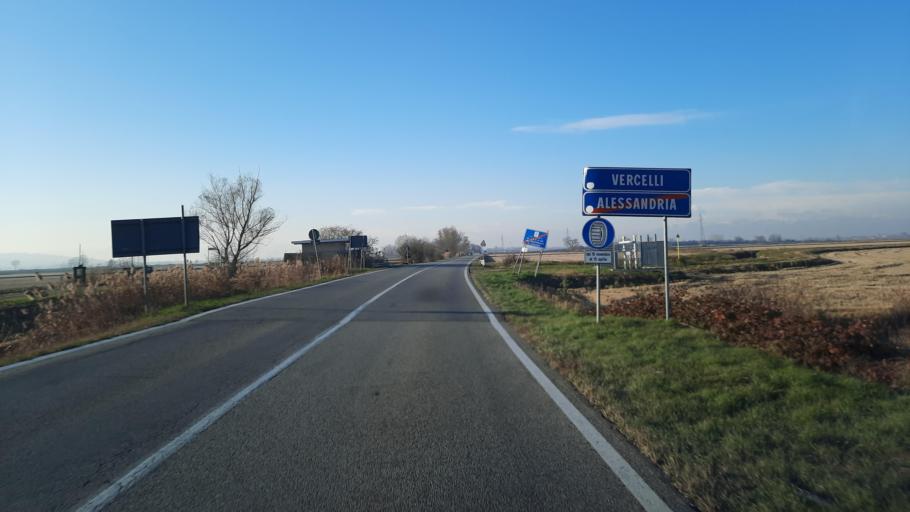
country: IT
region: Piedmont
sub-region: Provincia di Alessandria
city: Morano sul Po
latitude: 45.1719
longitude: 8.3429
